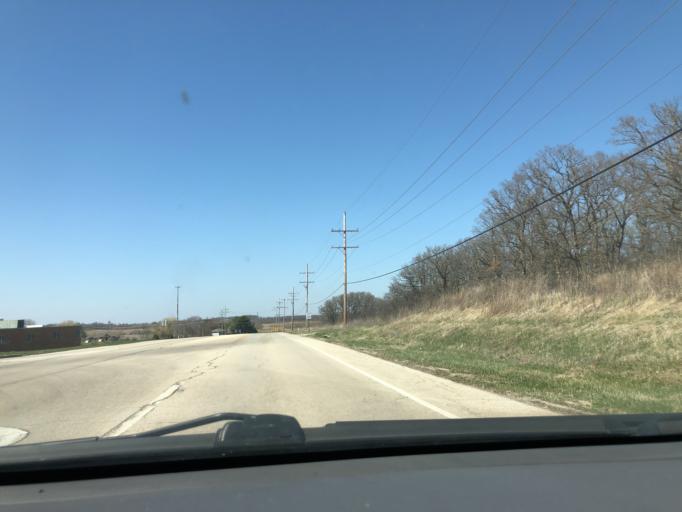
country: US
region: Illinois
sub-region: Kane County
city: Hampshire
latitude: 42.1194
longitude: -88.4912
